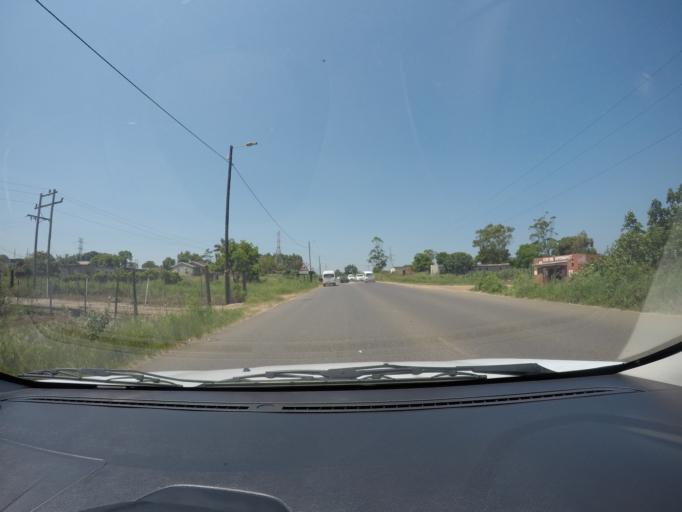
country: ZA
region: KwaZulu-Natal
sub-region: uThungulu District Municipality
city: eSikhawini
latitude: -28.8467
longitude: 31.9309
